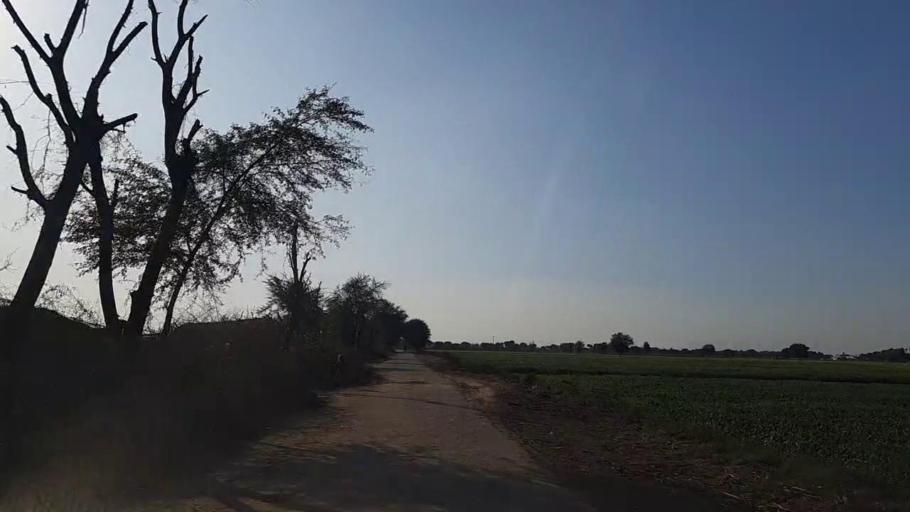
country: PK
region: Sindh
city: Shahpur Chakar
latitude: 26.1927
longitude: 68.6417
